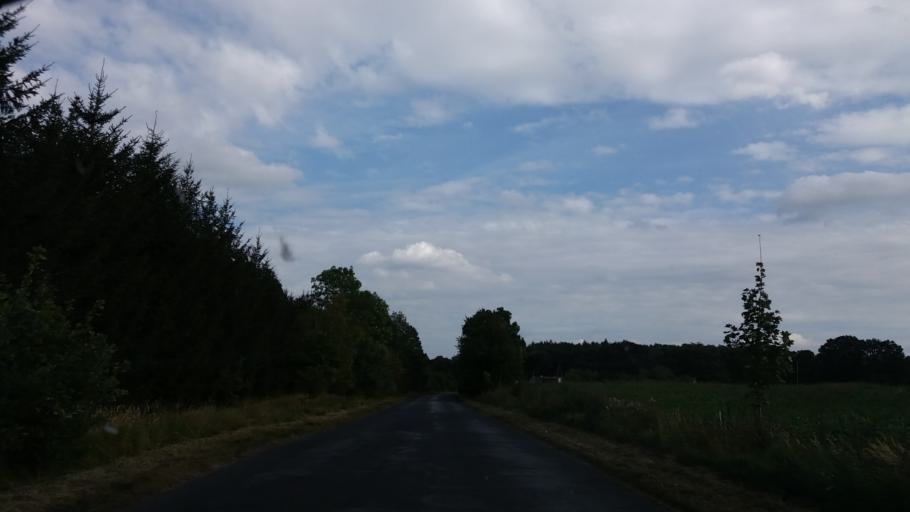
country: PL
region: West Pomeranian Voivodeship
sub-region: Powiat stargardzki
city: Dolice
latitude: 53.2420
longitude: 15.2327
